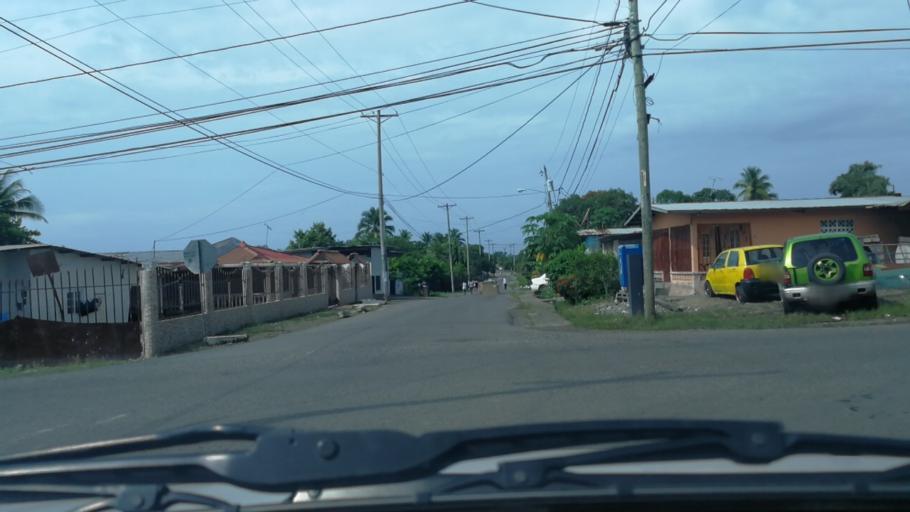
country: PA
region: Panama
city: Pacora
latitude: 9.0829
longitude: -79.2932
